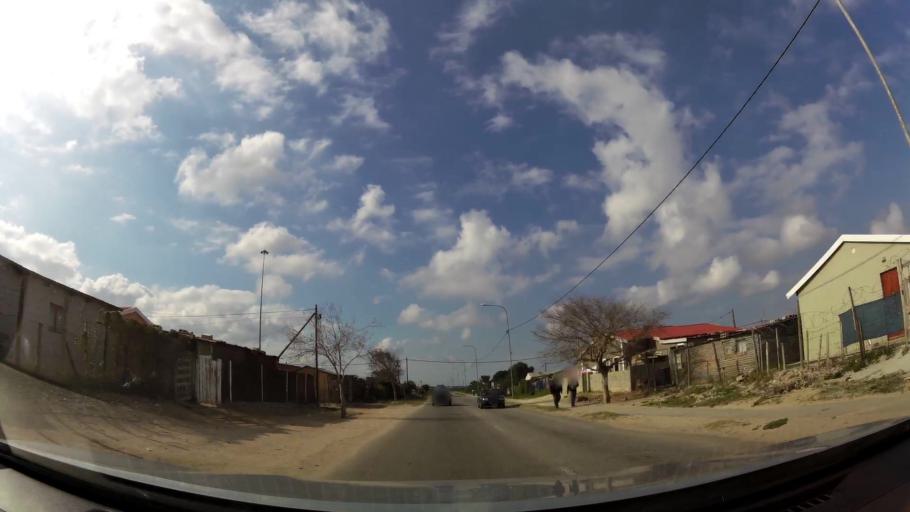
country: ZA
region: Eastern Cape
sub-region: Nelson Mandela Bay Metropolitan Municipality
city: Port Elizabeth
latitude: -33.7871
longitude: 25.5880
